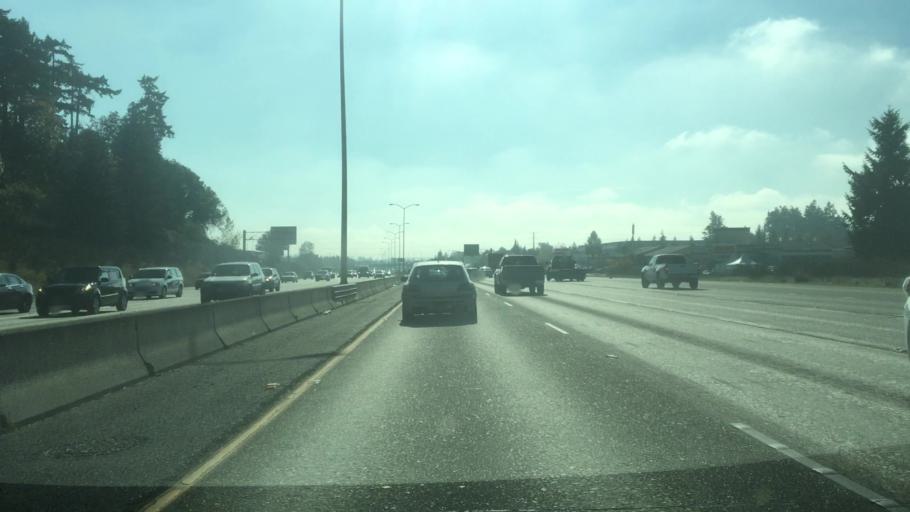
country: US
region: Washington
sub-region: Pierce County
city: Parkland
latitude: 47.1978
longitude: -122.4621
